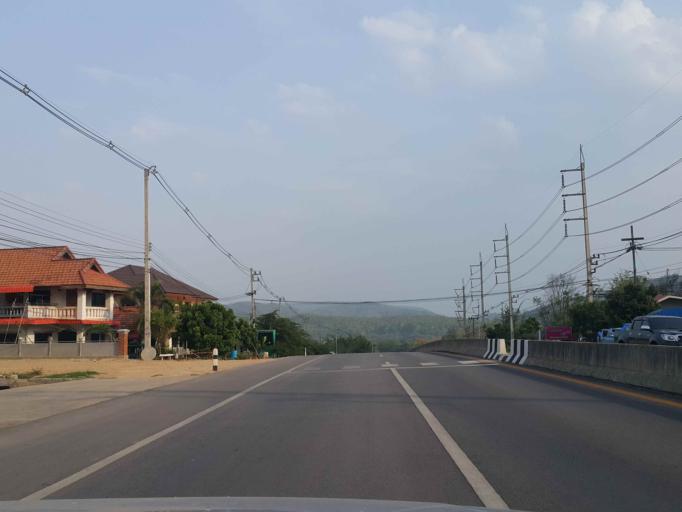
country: TH
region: Chiang Mai
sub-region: Amphoe Chiang Dao
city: Chiang Dao
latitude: 19.3201
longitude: 98.9556
